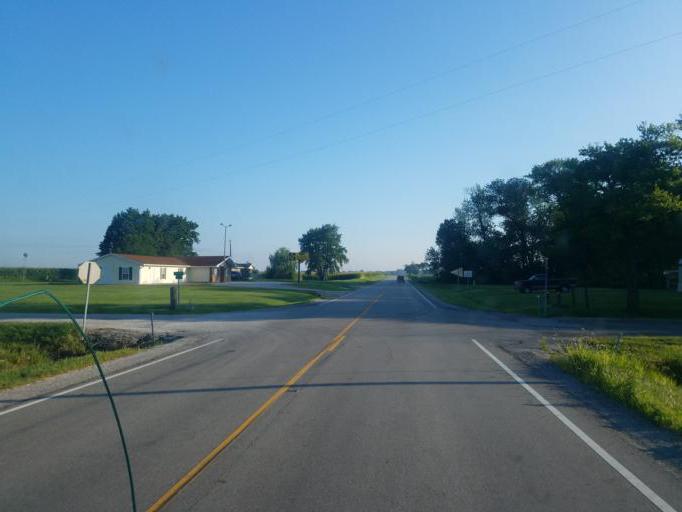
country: US
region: Illinois
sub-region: Bond County
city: Greenville
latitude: 38.8434
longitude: -89.3712
